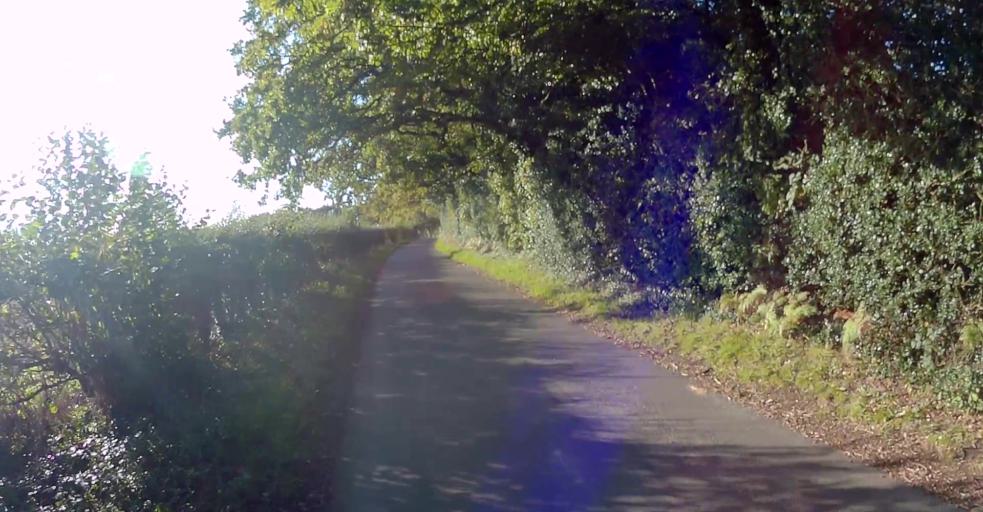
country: GB
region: England
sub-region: Surrey
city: Farnham
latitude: 51.2126
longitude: -0.8656
